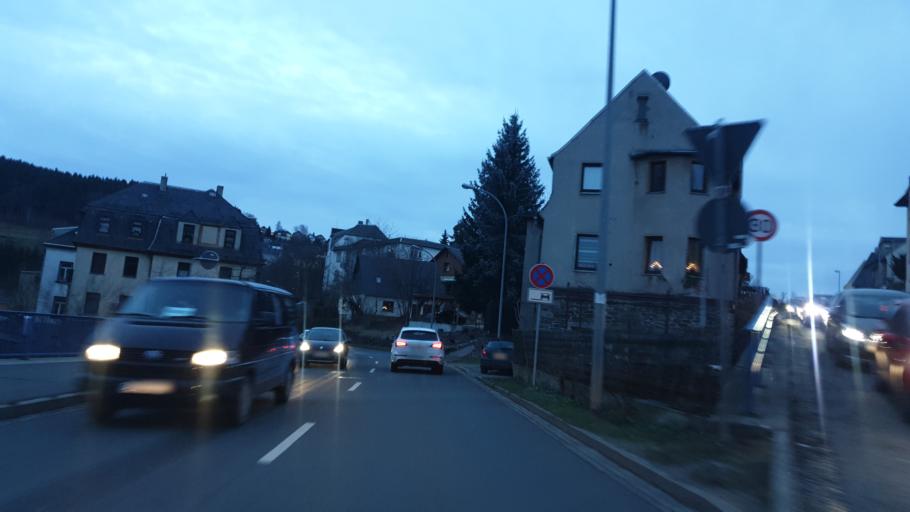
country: DE
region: Saxony
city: Schneeberg
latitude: 50.5910
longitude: 12.6401
